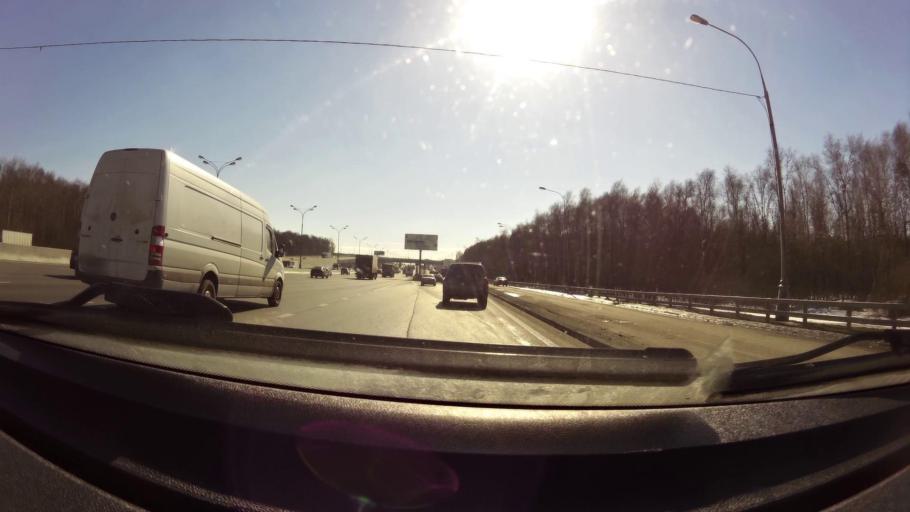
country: RU
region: Moskovskaya
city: Vostryakovo
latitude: 55.6443
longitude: 37.4528
